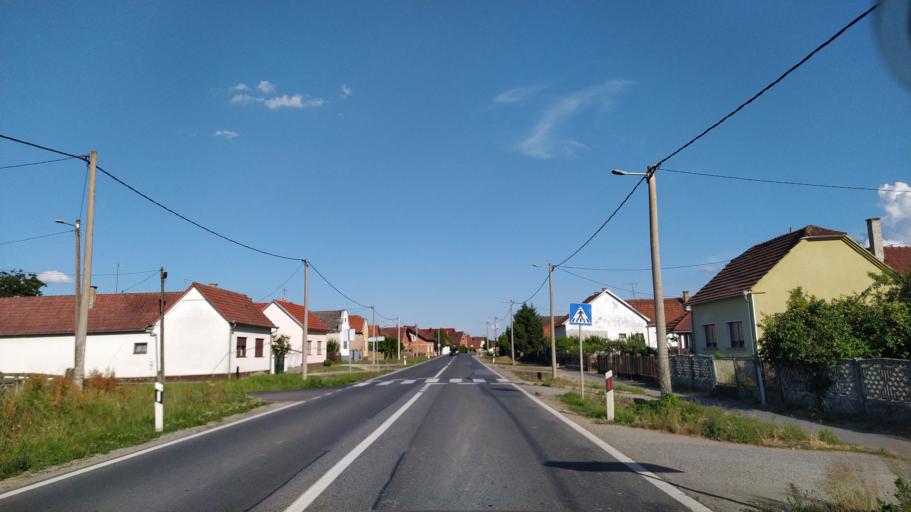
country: HR
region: Virovitick-Podravska
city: Spisic-Bukovica
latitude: 45.8702
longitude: 17.2944
